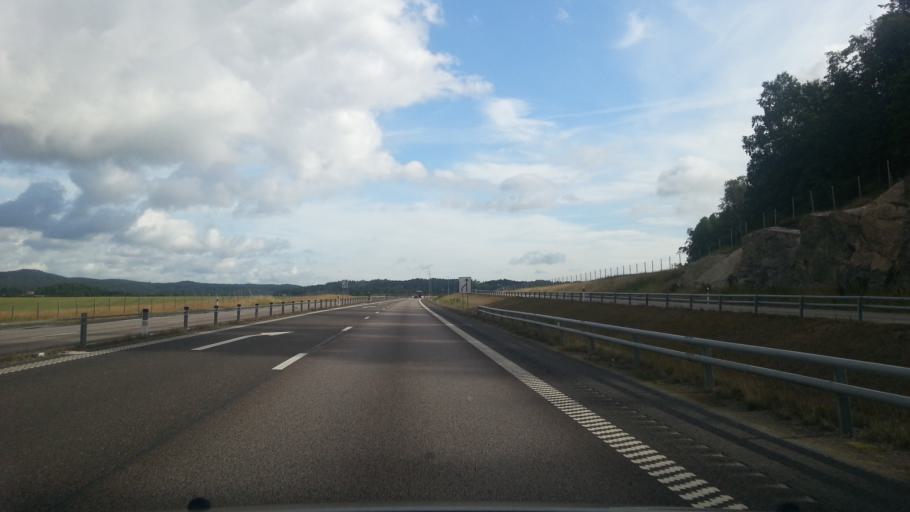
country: SE
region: Vaestra Goetaland
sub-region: Lilla Edets Kommun
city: Lilla Edet
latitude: 58.1944
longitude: 12.1486
